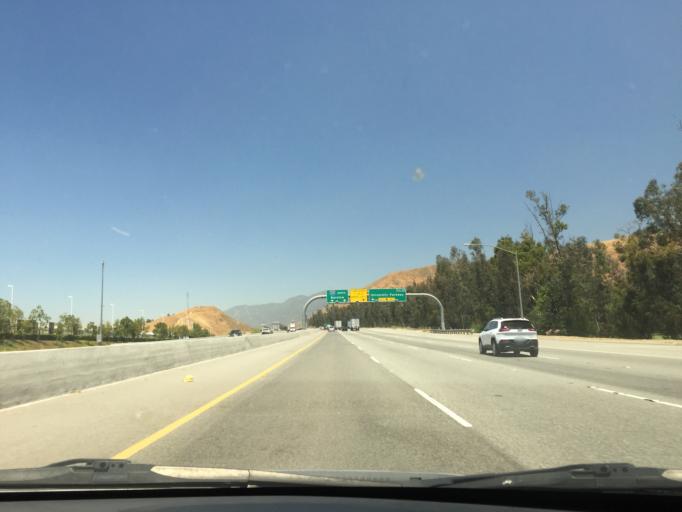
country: US
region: California
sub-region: San Bernardino County
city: Muscoy
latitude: 34.1535
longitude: -117.3246
